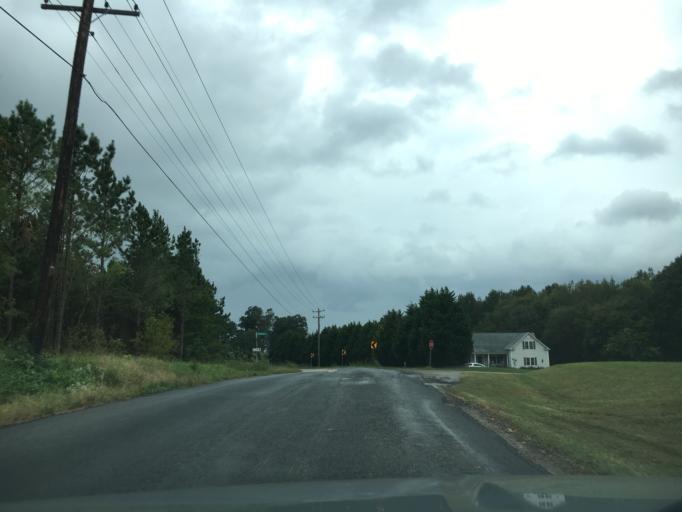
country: US
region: Virginia
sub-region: Amelia County
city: Amelia Court House
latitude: 37.3756
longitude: -77.9766
